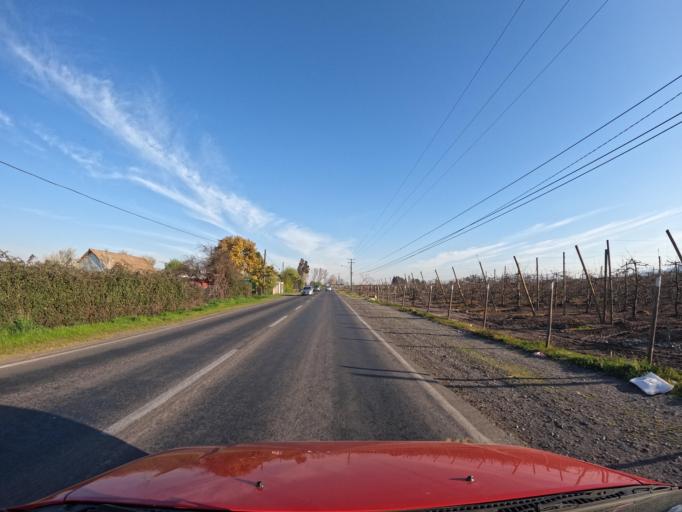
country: CL
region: Maule
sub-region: Provincia de Curico
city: Rauco
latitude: -34.8950
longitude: -71.2738
